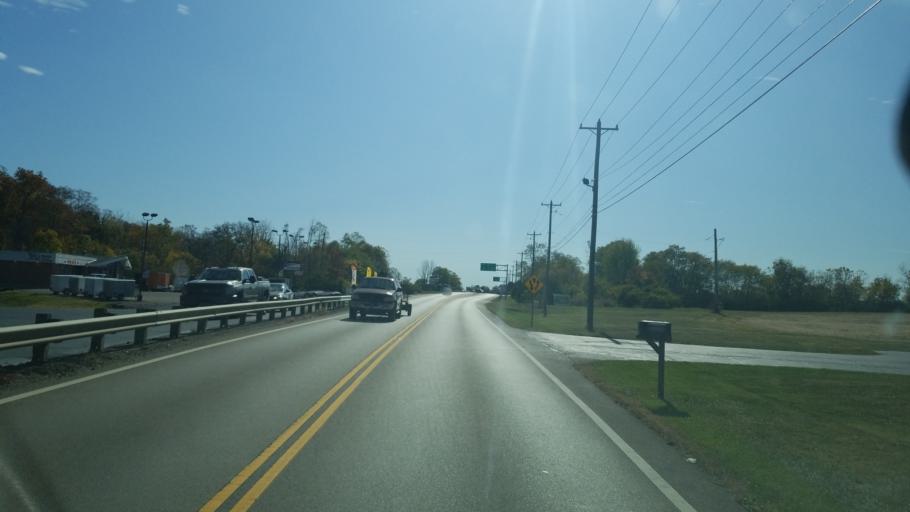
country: US
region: Ohio
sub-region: Warren County
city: Lebanon
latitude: 39.4165
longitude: -84.1559
